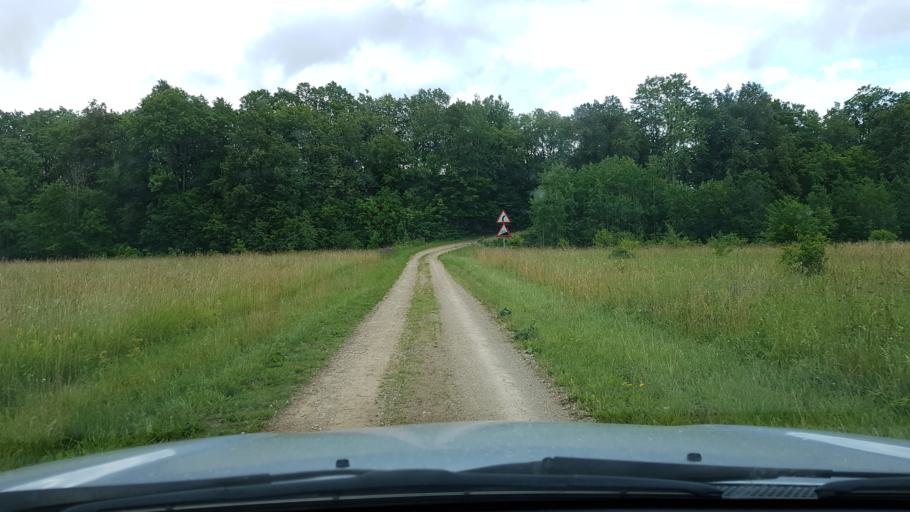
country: EE
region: Ida-Virumaa
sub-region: Narva-Joesuu linn
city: Narva-Joesuu
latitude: 59.4029
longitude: 27.9731
